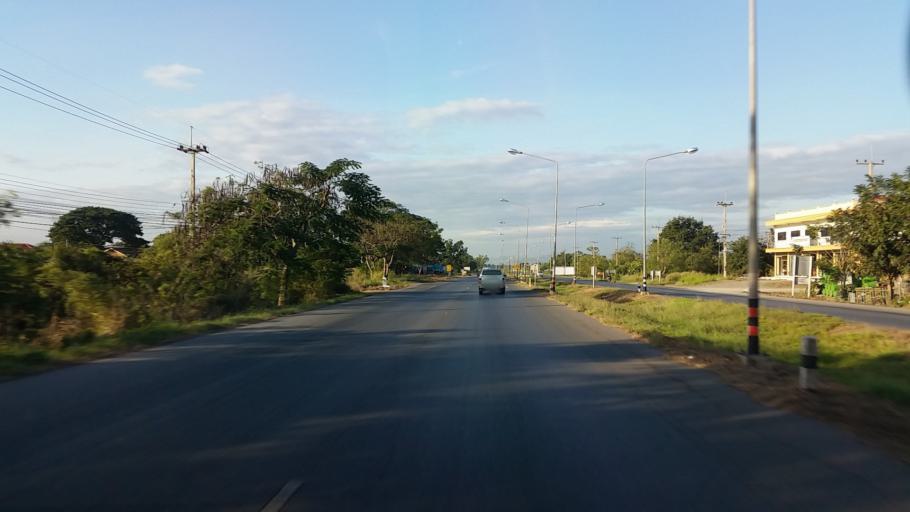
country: TH
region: Lop Buri
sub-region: Amphoe Tha Luang
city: Tha Luang
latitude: 15.0762
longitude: 100.9943
